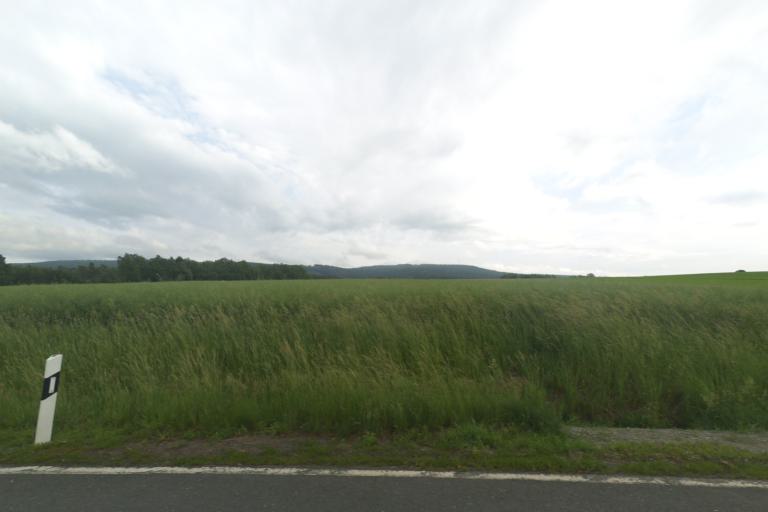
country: DE
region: Bavaria
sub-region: Upper Franconia
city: Sparneck
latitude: 50.1610
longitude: 11.8254
